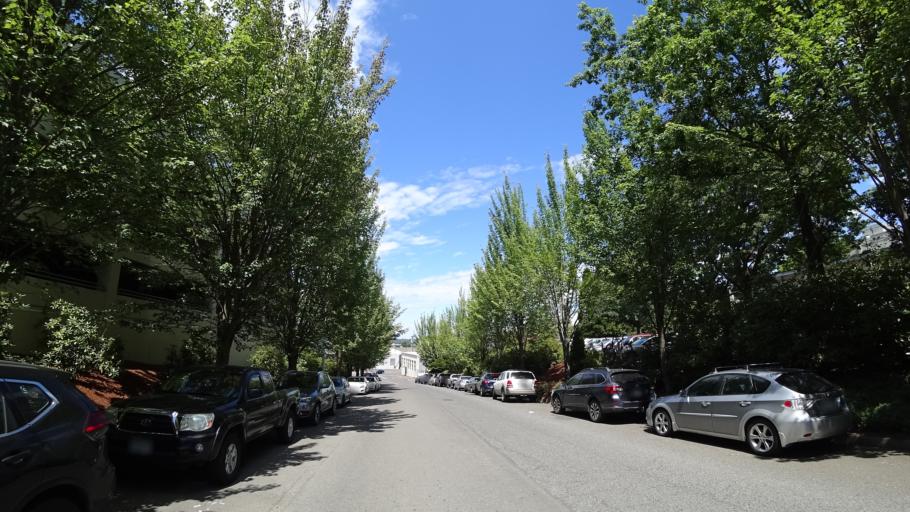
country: US
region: Oregon
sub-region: Multnomah County
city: Portland
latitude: 45.5384
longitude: -122.7070
